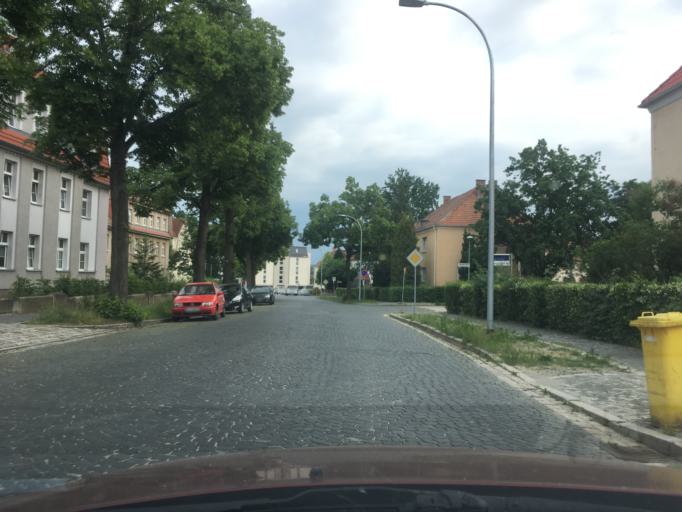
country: DE
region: Saxony
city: Bautzen
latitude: 51.1750
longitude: 14.4446
